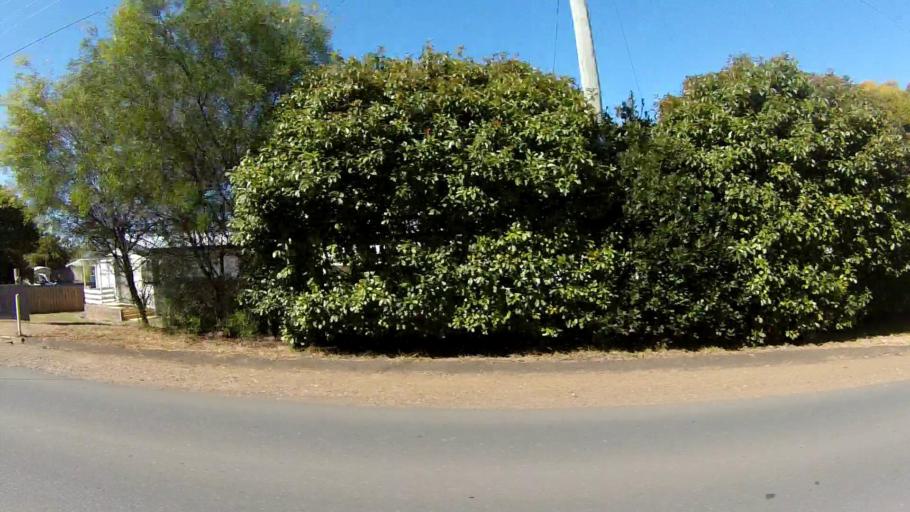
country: AU
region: Tasmania
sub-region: Sorell
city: Sorell
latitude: -42.5565
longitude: 147.8714
